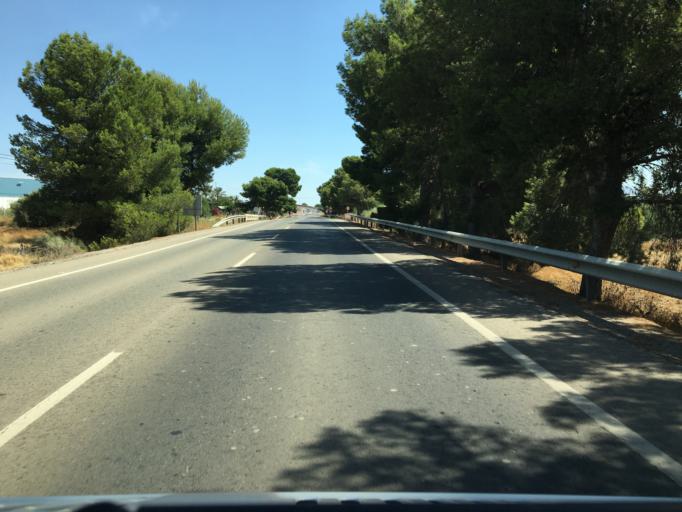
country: ES
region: Andalusia
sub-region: Provincia de Almeria
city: Huercal-Overa
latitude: 37.4311
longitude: -1.9123
